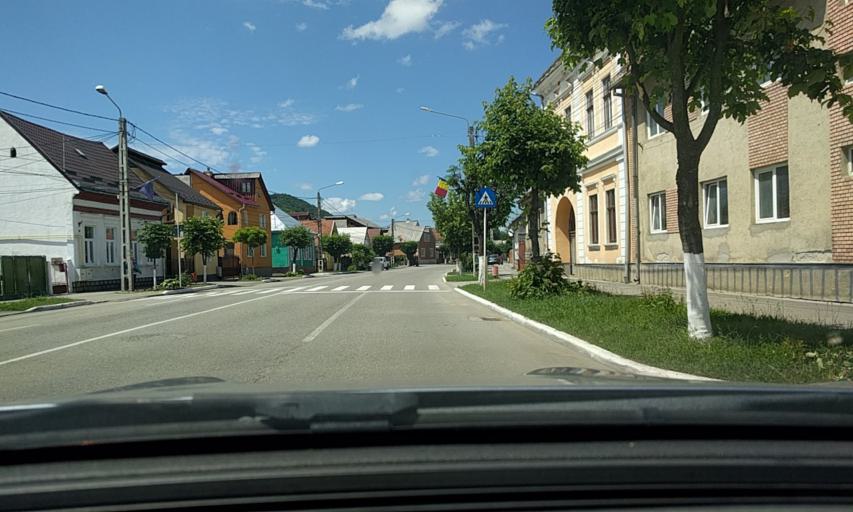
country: RO
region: Bistrita-Nasaud
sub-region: Oras Nasaud
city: Nasaud
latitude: 47.2870
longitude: 24.3972
